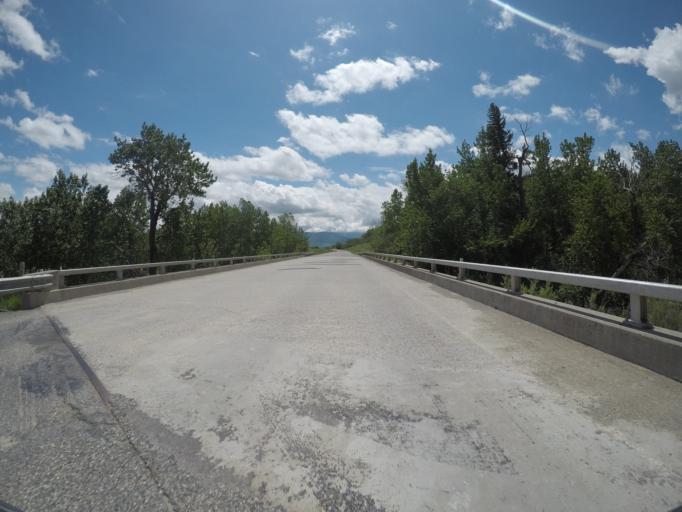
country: US
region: Montana
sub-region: Sweet Grass County
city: Big Timber
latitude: 45.6612
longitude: -110.1134
